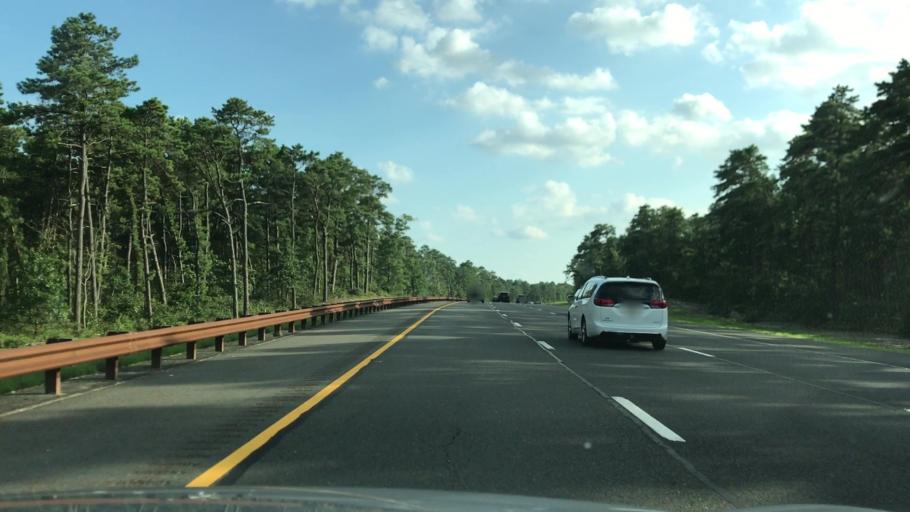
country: US
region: New Jersey
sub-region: Ocean County
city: Manahawkin
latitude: 39.6850
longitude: -74.3030
